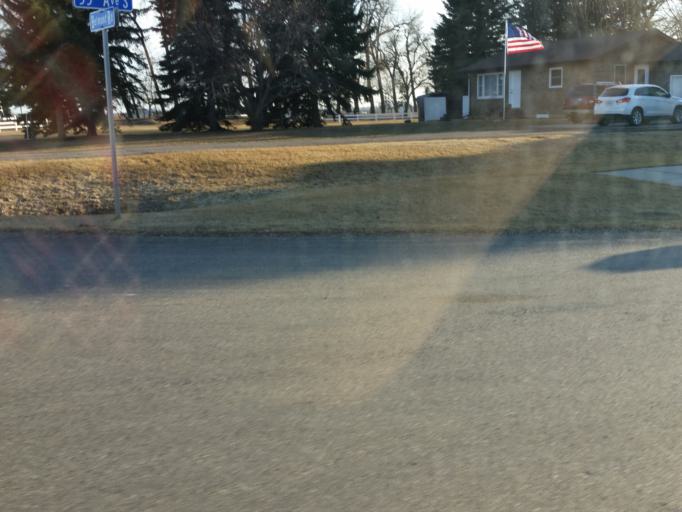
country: US
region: North Dakota
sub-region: Grand Forks County
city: Grand Forks
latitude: 47.8667
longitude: -97.0292
